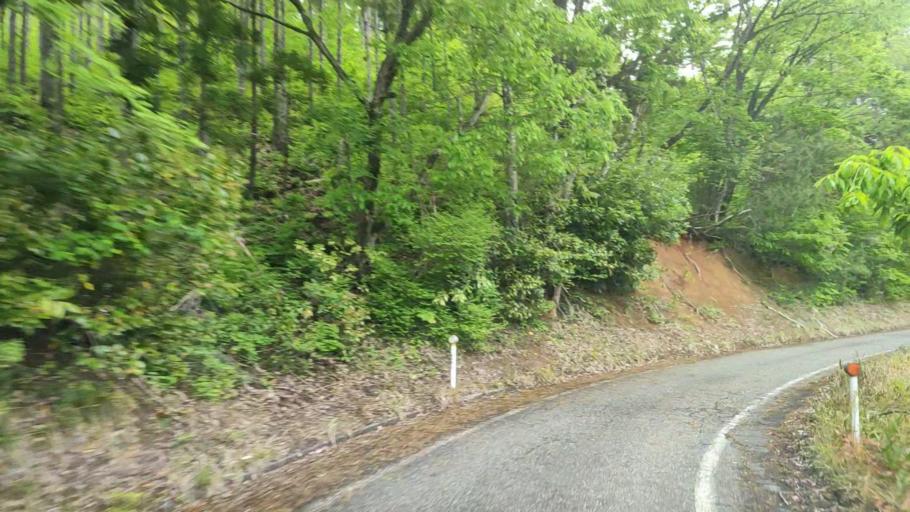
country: JP
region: Niigata
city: Kamo
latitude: 37.7165
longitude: 139.0858
